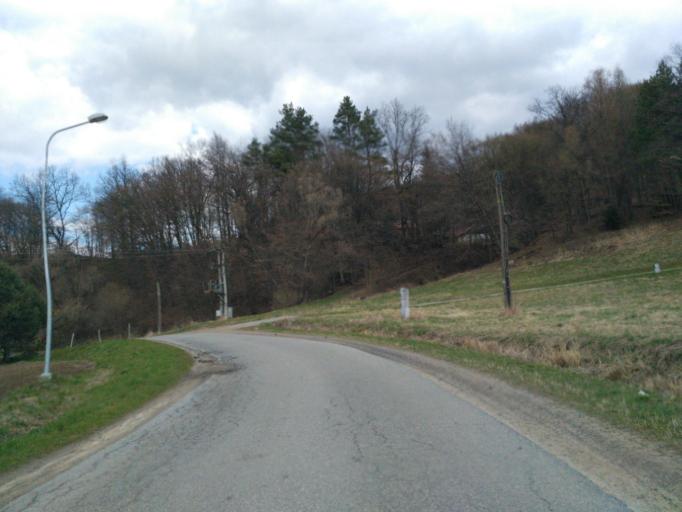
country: PL
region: Subcarpathian Voivodeship
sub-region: Powiat sanocki
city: Tyrawa Woloska
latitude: 49.6590
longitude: 22.3005
